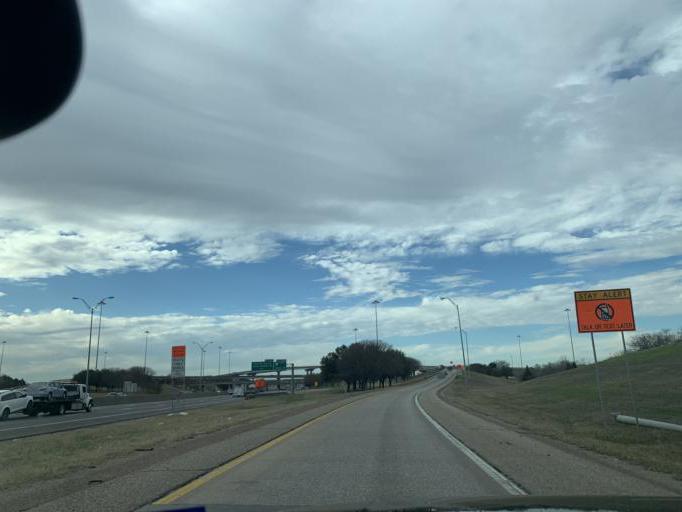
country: US
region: Texas
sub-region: Dallas County
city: Duncanville
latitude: 32.6521
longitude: -96.8722
